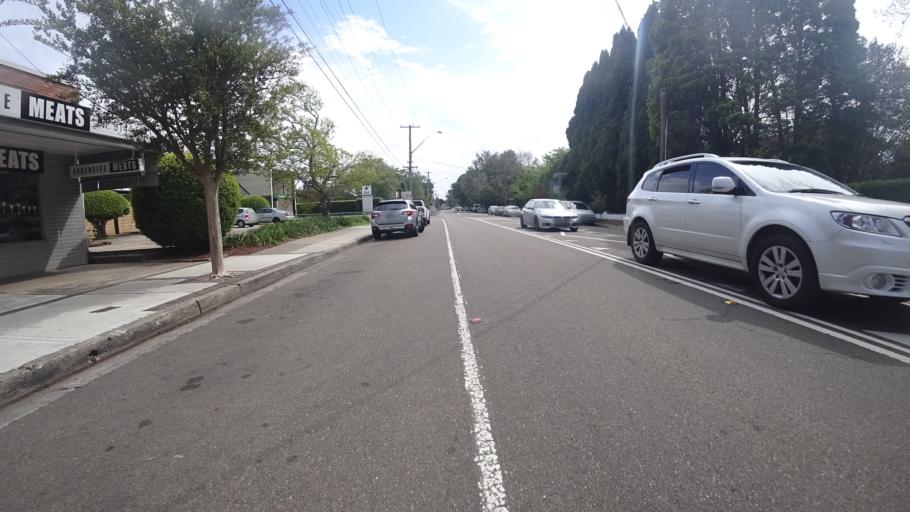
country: AU
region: New South Wales
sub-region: City of Sydney
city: North Turramurra
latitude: -33.7129
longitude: 151.1472
